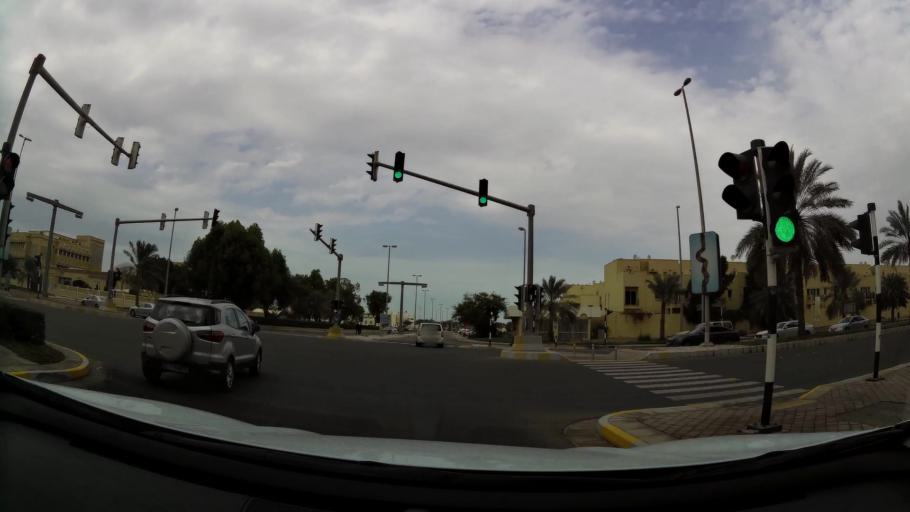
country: AE
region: Abu Dhabi
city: Abu Dhabi
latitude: 24.4212
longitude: 54.4406
